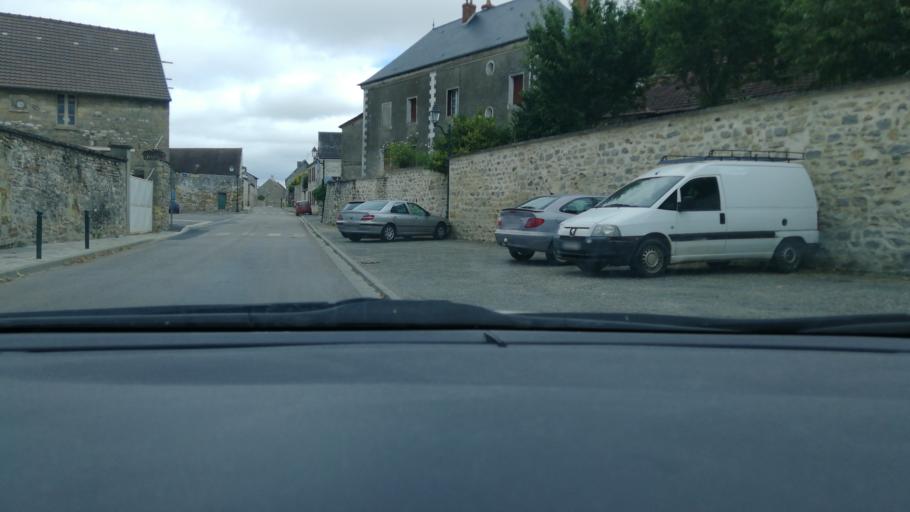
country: FR
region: Ile-de-France
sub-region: Departement du Val-d'Oise
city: Osny
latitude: 49.0887
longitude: 2.0678
